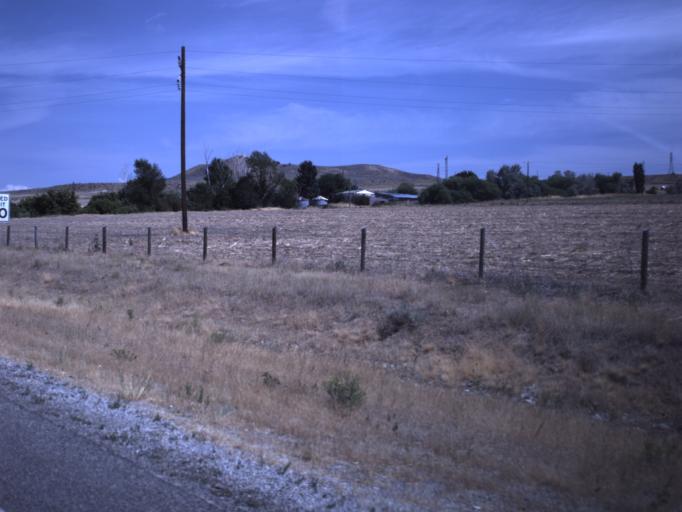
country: US
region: Utah
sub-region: Box Elder County
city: Garland
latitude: 41.7870
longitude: -112.0835
